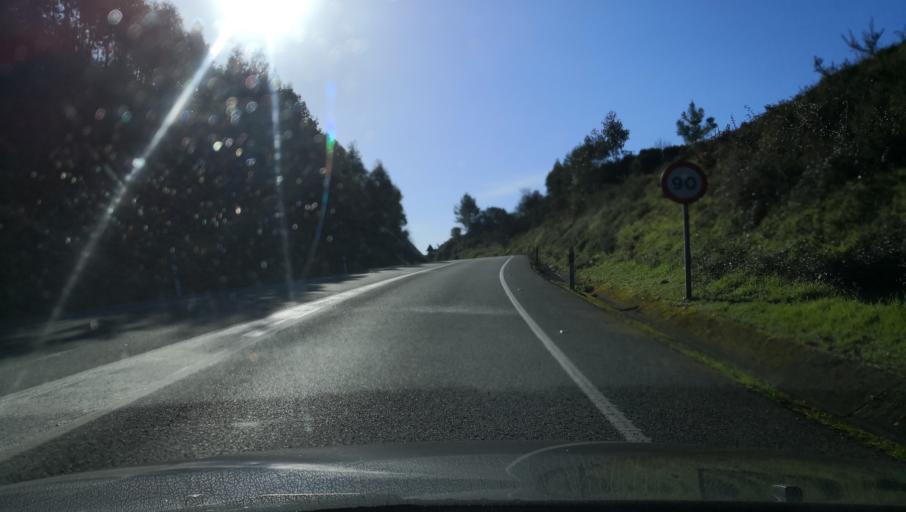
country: ES
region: Galicia
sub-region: Provincia da Coruna
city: Vedra
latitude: 42.7900
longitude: -8.4434
